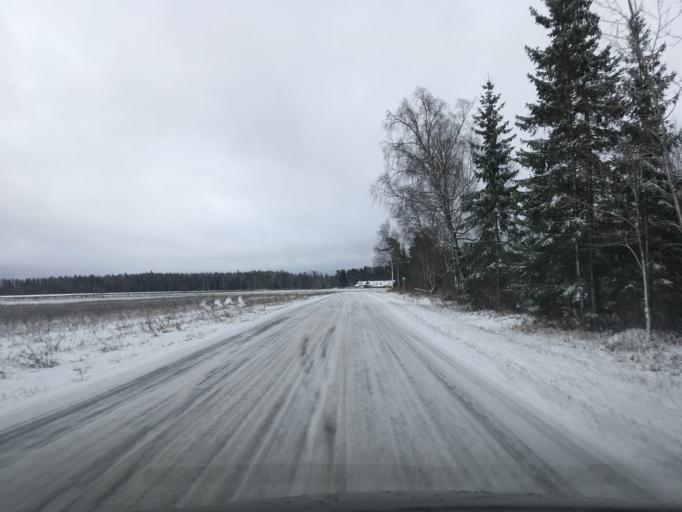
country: EE
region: Harju
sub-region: Raasiku vald
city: Raasiku
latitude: 59.2154
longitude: 25.1818
